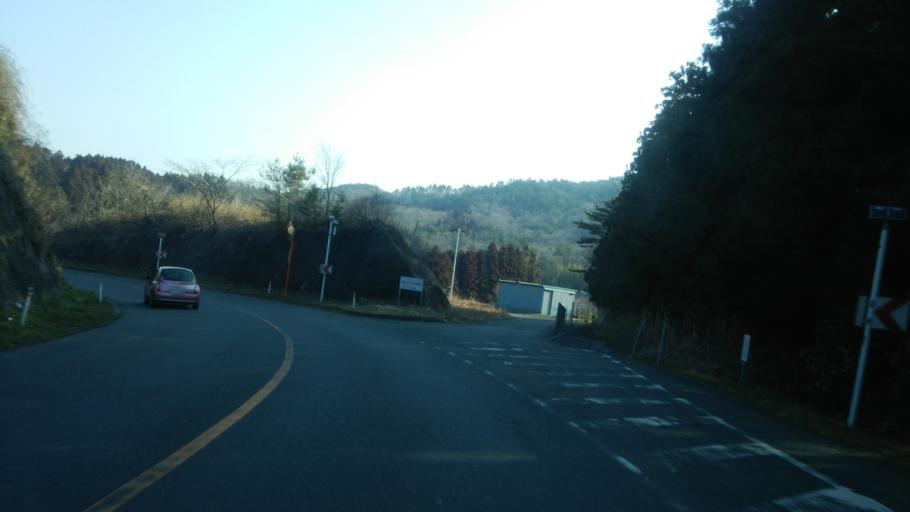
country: JP
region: Fukushima
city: Iwaki
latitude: 37.0559
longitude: 140.8029
